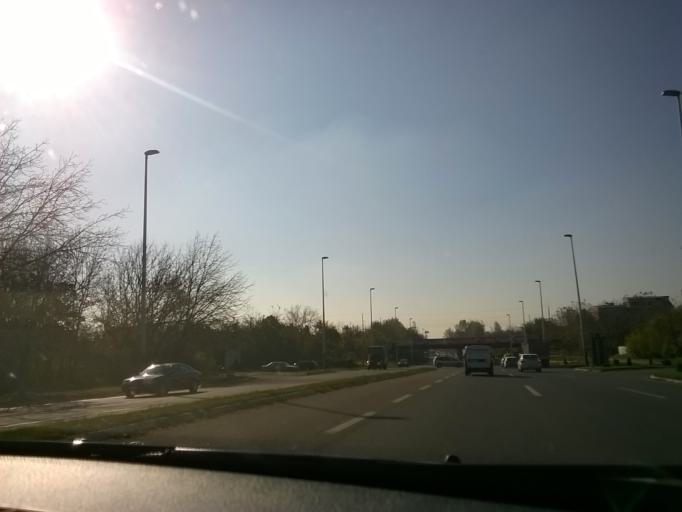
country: RS
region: Central Serbia
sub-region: Belgrade
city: Zemun
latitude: 44.8401
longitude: 20.3666
